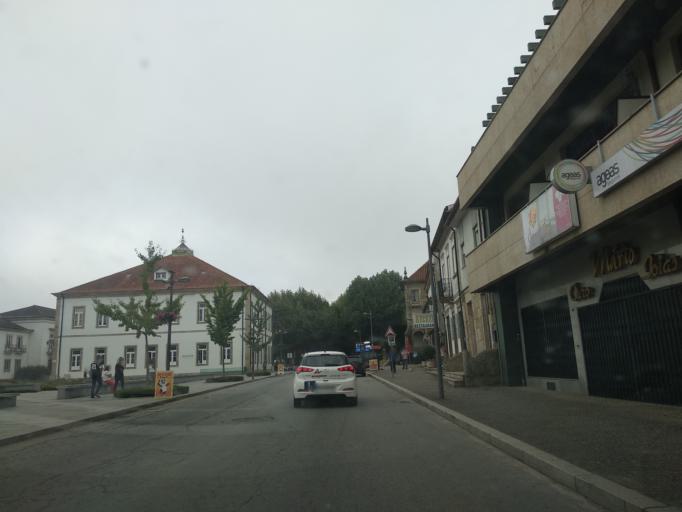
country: PT
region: Braga
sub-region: Vila Verde
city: Vila Verde
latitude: 41.6485
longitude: -8.4361
